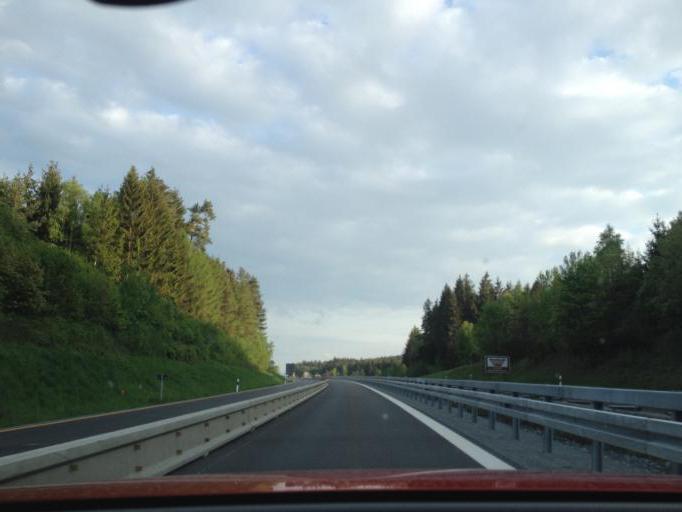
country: DE
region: Bavaria
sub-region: Upper Palatinate
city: Windischeschenbach
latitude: 49.7666
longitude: 12.1519
